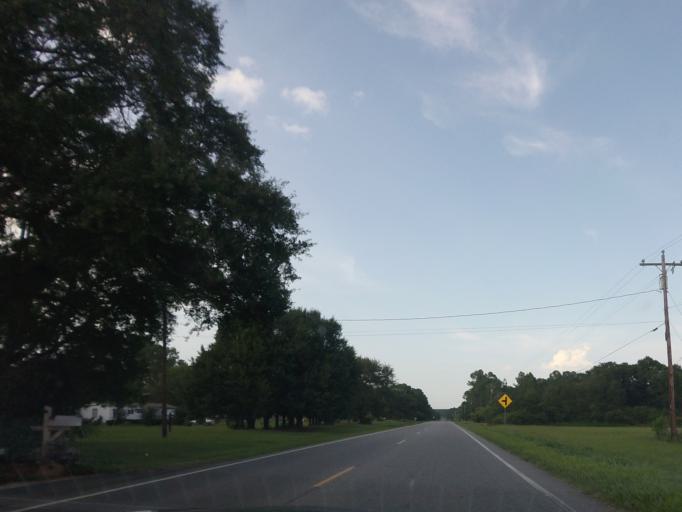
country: US
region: Georgia
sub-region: Bleckley County
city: Cochran
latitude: 32.4248
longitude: -83.3111
